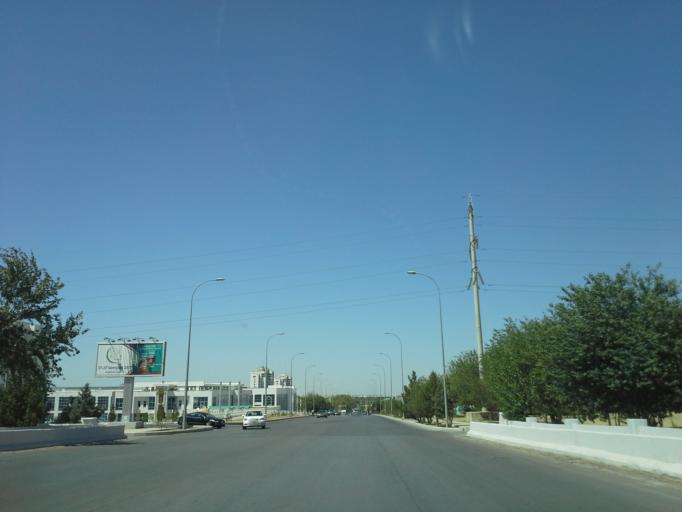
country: TM
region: Ahal
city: Ashgabat
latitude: 37.9057
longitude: 58.4059
